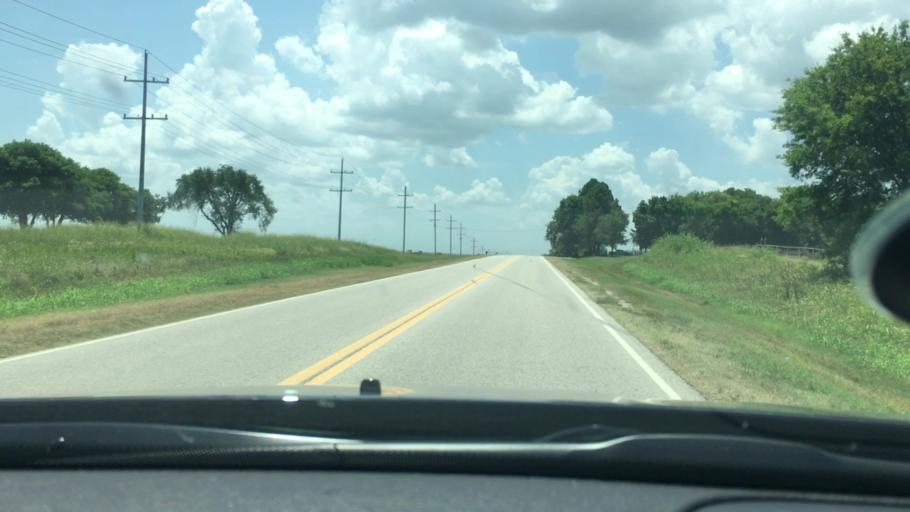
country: US
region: Oklahoma
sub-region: Pontotoc County
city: Ada
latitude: 34.6744
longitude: -96.6349
